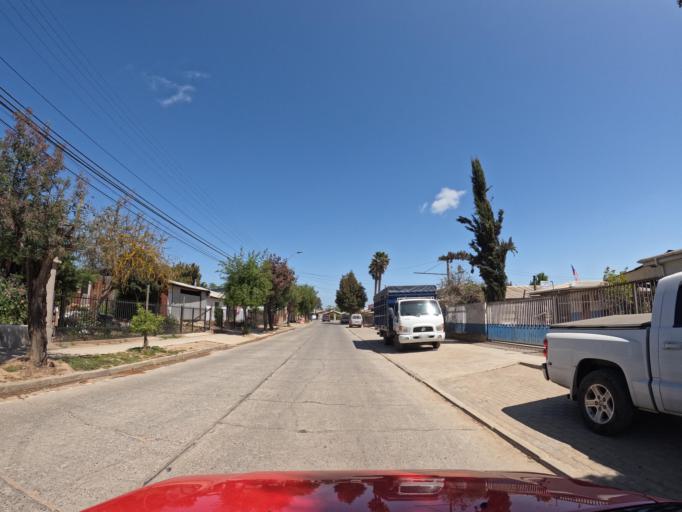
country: CL
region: O'Higgins
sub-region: Provincia de Colchagua
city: Santa Cruz
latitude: -34.7286
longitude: -71.6497
